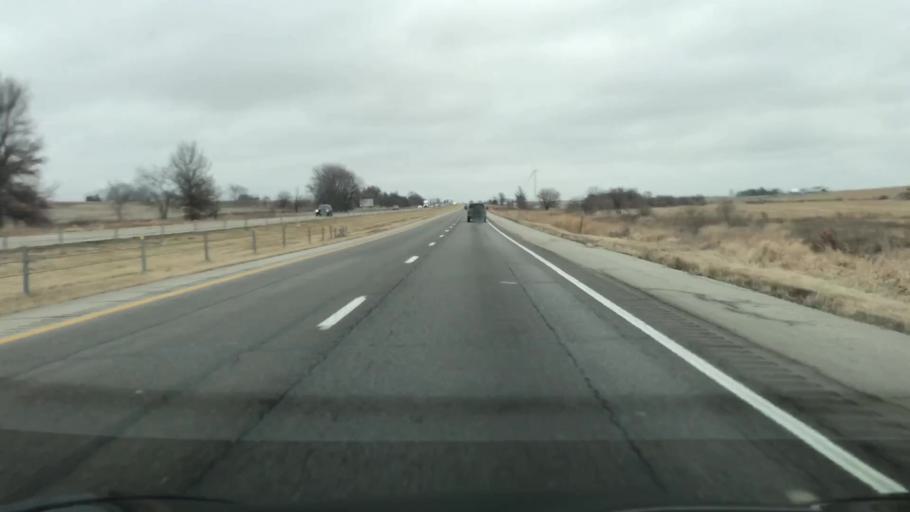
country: US
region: Iowa
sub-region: Guthrie County
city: Stuart
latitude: 41.4929
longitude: -94.2846
